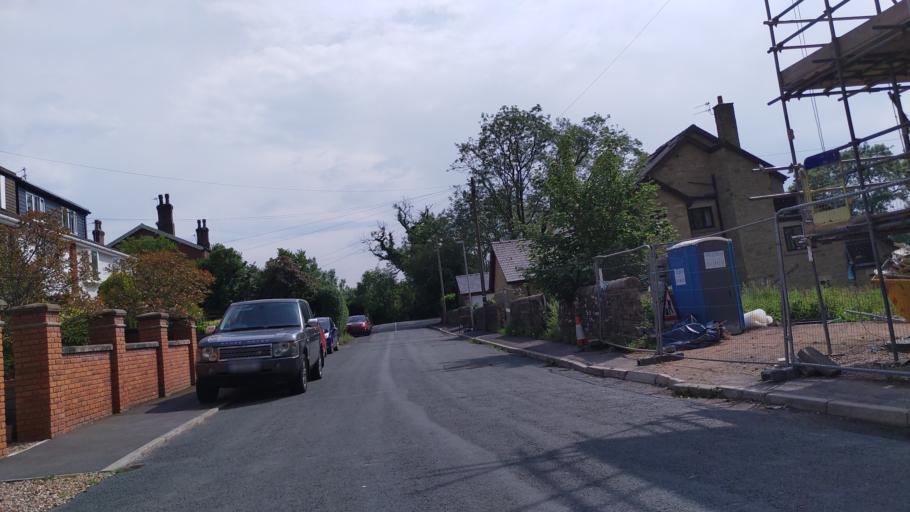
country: GB
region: England
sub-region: Lancashire
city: Chorley
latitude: 53.6794
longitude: -2.6197
